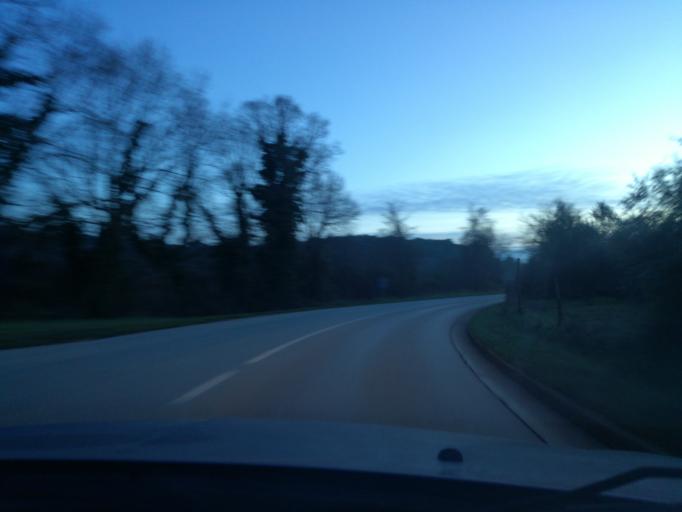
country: HR
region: Istarska
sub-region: Grad Rovinj
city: Rovinj
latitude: 45.1006
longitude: 13.6443
